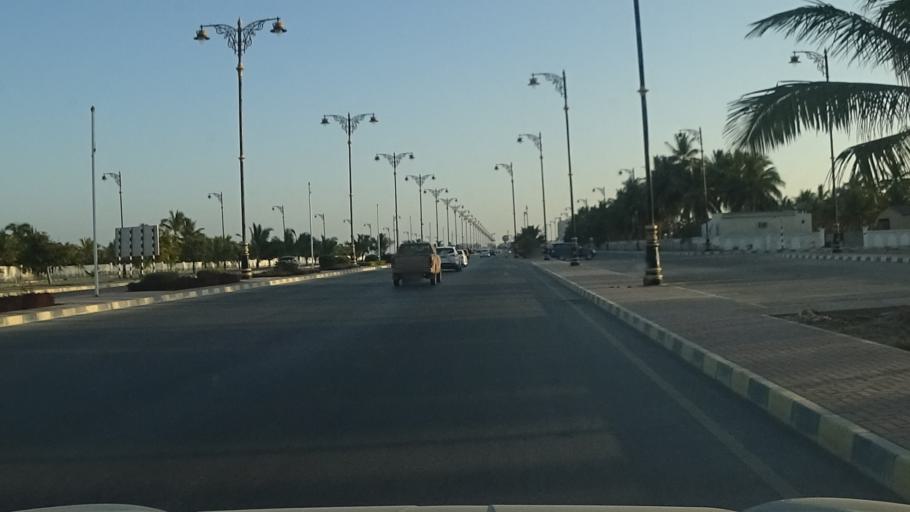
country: OM
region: Zufar
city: Salalah
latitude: 17.0344
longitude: 54.1720
